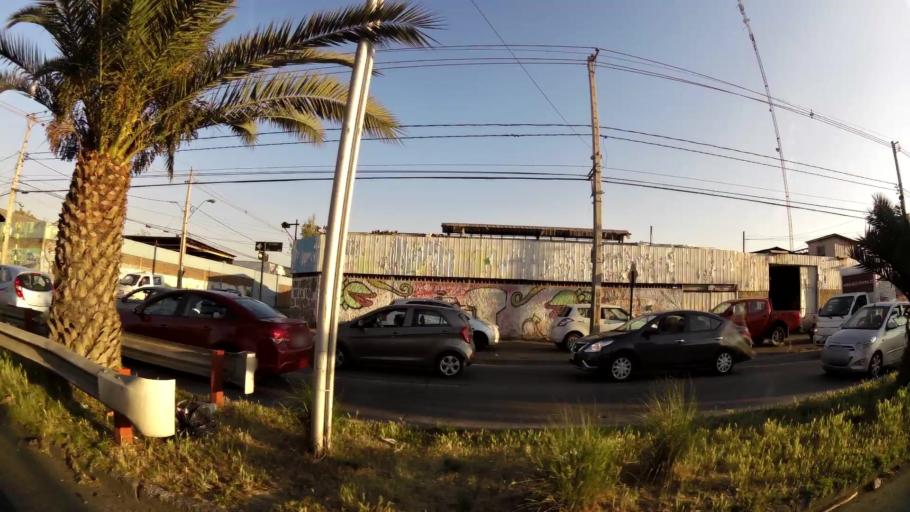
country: CL
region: Santiago Metropolitan
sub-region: Provincia de Santiago
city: La Pintana
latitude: -33.5239
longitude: -70.6212
